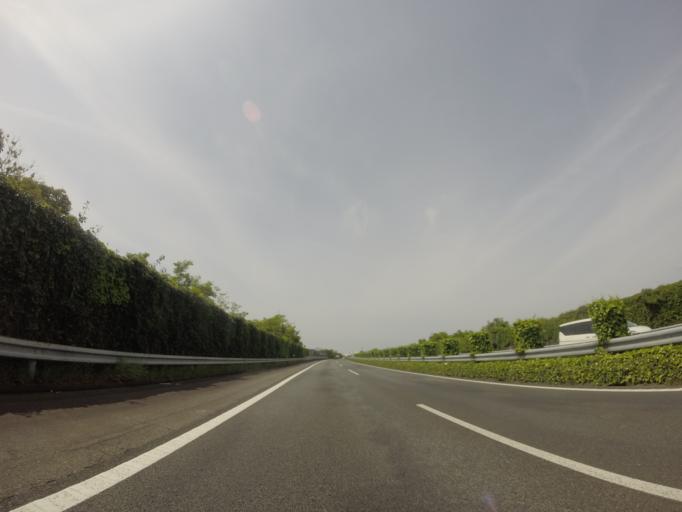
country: JP
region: Shizuoka
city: Fujieda
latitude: 34.8714
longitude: 138.2917
